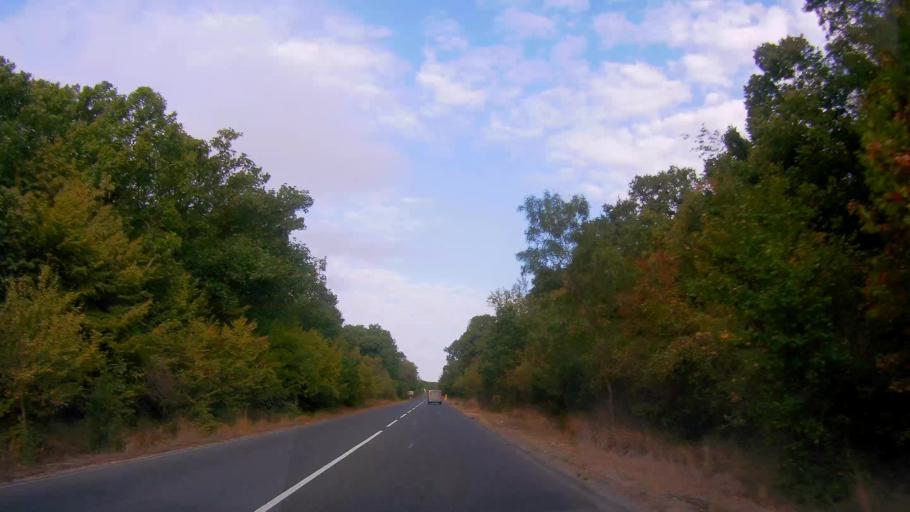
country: BG
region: Burgas
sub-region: Obshtina Primorsko
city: Primorsko
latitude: 42.3338
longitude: 27.7246
